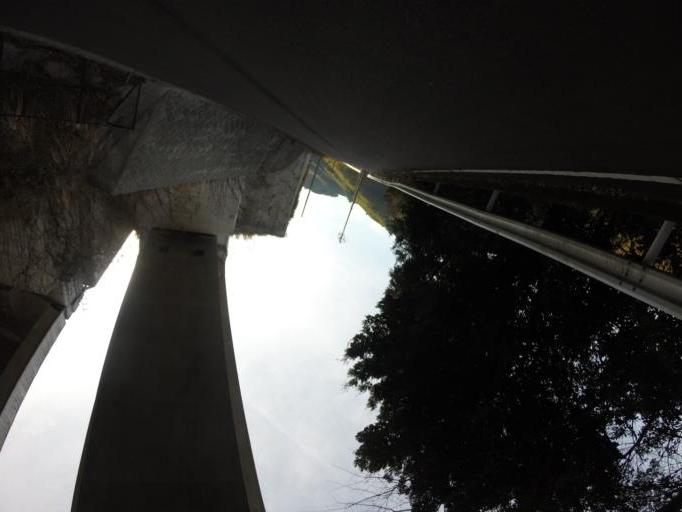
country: JP
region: Shizuoka
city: Shizuoka-shi
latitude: 35.0738
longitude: 138.4608
